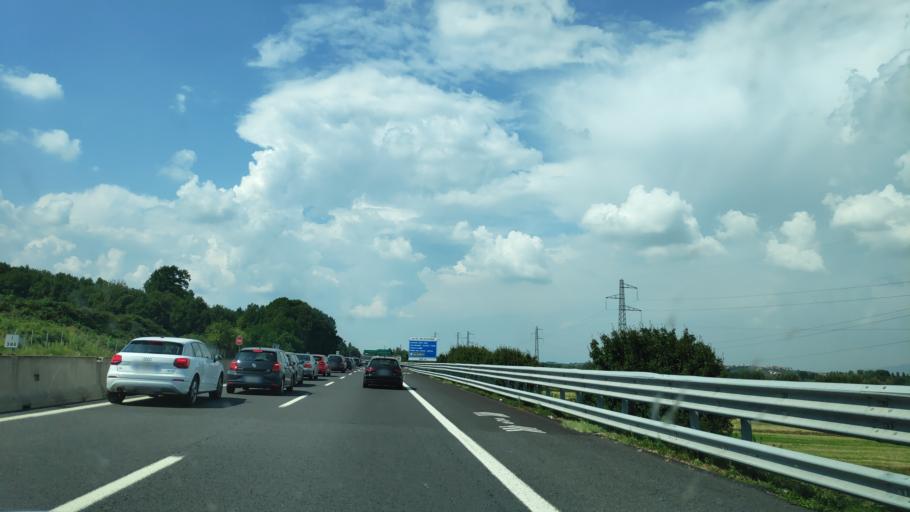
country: IT
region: Tuscany
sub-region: Provincia di Siena
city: Bettolle
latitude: 43.2060
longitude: 11.8133
